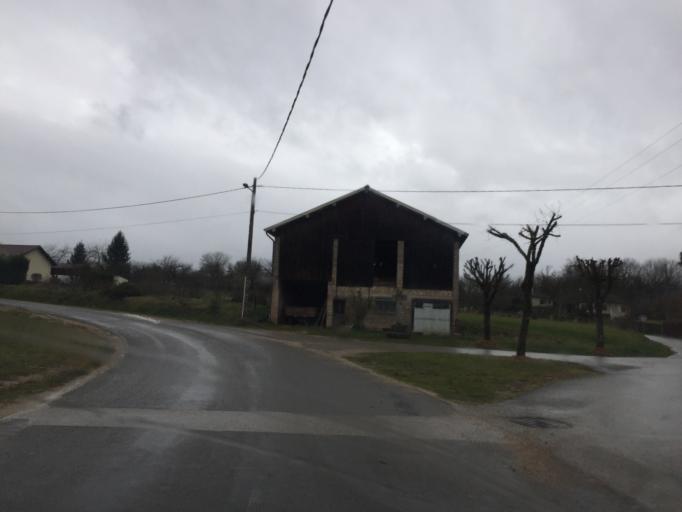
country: FR
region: Franche-Comte
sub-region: Departement du Jura
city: Dole
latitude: 47.1454
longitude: 5.5488
